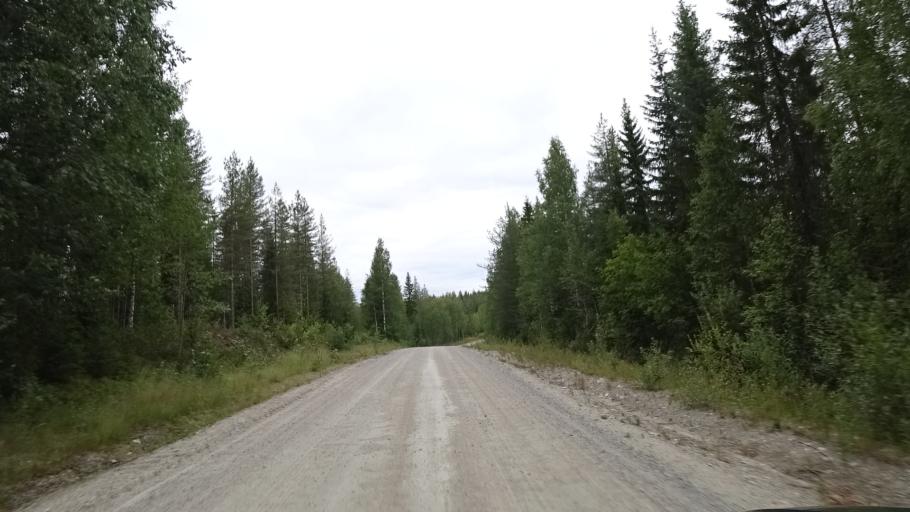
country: FI
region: North Karelia
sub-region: Joensuu
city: Eno
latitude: 63.1569
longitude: 30.5946
